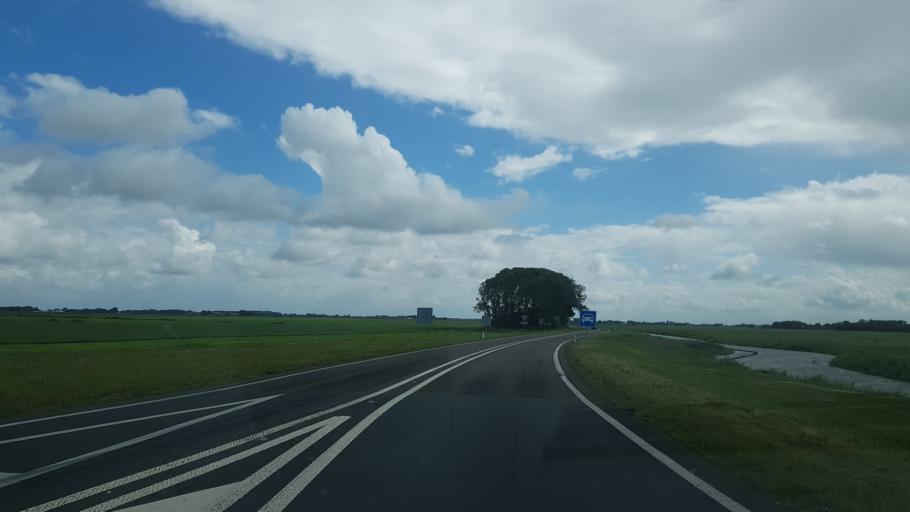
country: NL
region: Friesland
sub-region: Gemeente Dongeradeel
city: Dokkum
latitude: 53.3329
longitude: 6.0276
